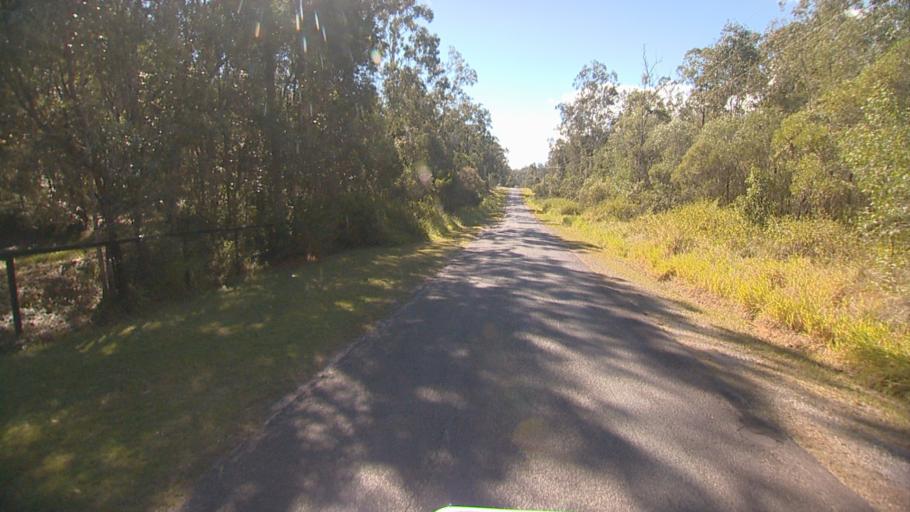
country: AU
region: Queensland
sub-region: Logan
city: Chambers Flat
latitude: -27.8087
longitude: 153.0822
